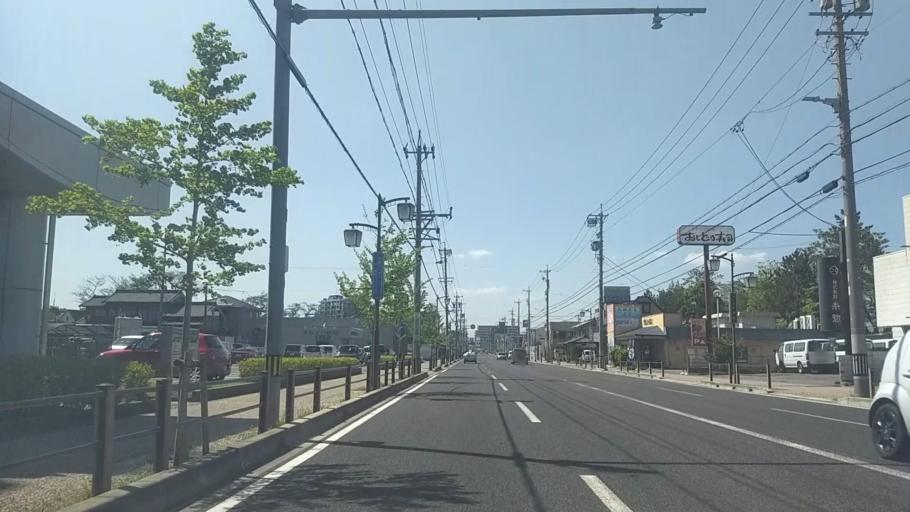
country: JP
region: Aichi
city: Okazaki
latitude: 34.9690
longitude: 137.1757
